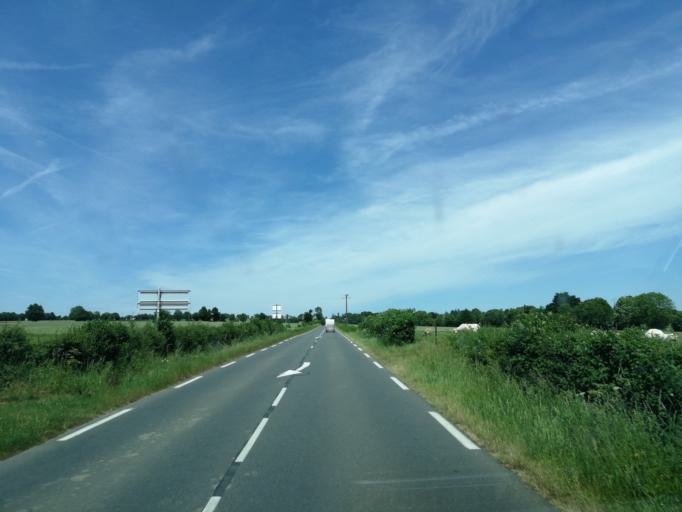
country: FR
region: Pays de la Loire
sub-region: Departement de la Vendee
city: La Tardiere
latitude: 46.6678
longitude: -0.7248
